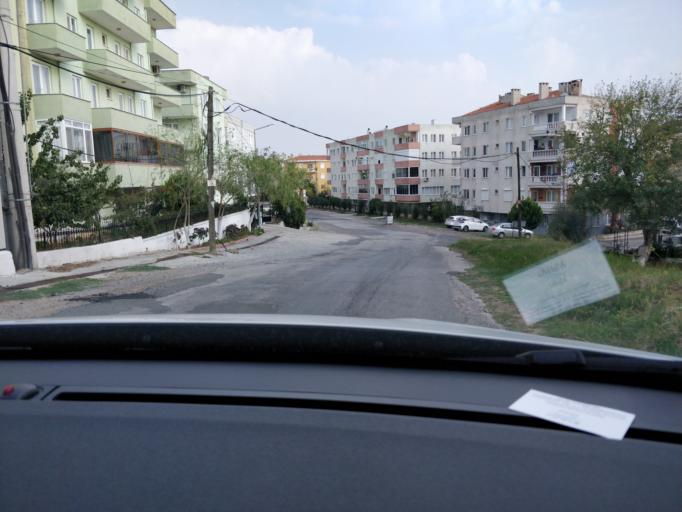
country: TR
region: Balikesir
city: Ayvalik
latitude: 39.2734
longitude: 26.6510
